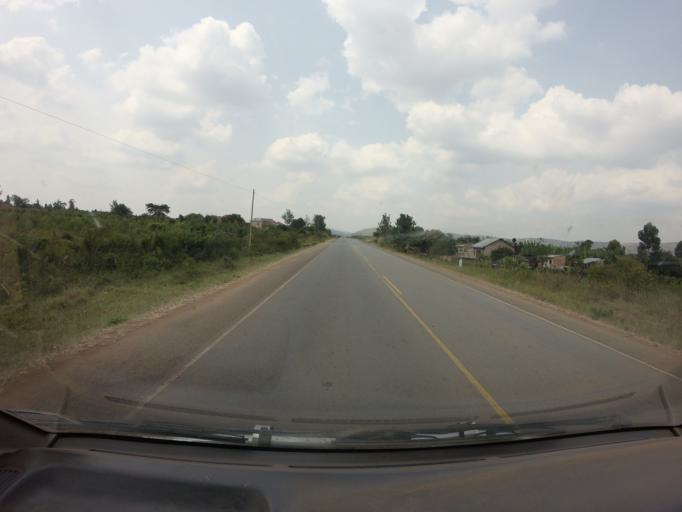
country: UG
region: Central Region
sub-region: Lyantonde District
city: Lyantonde
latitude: -0.3994
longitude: 31.1681
